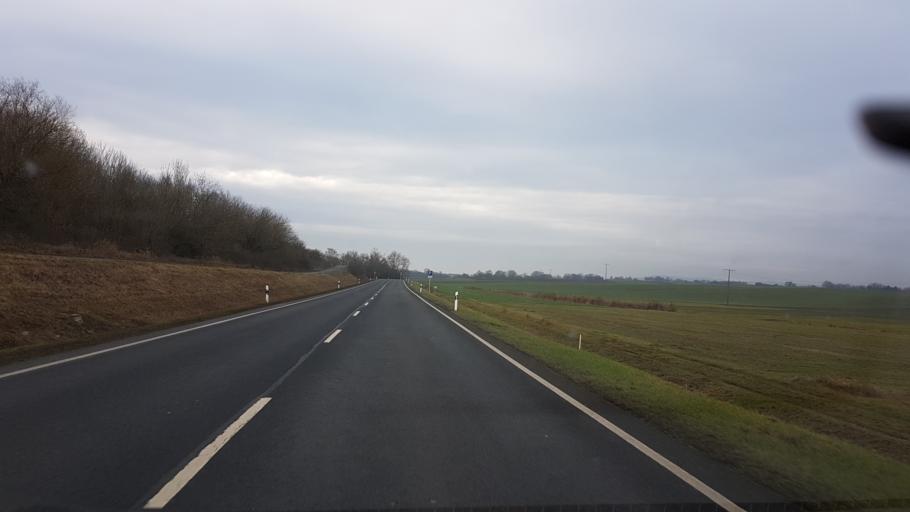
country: DE
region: Bavaria
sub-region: Regierungsbezirk Unterfranken
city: Ermershausen
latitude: 50.2354
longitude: 10.5686
